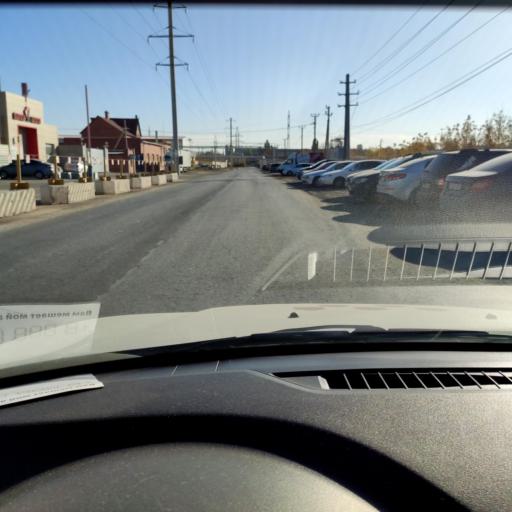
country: RU
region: Samara
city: Tol'yatti
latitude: 53.5458
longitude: 49.4378
